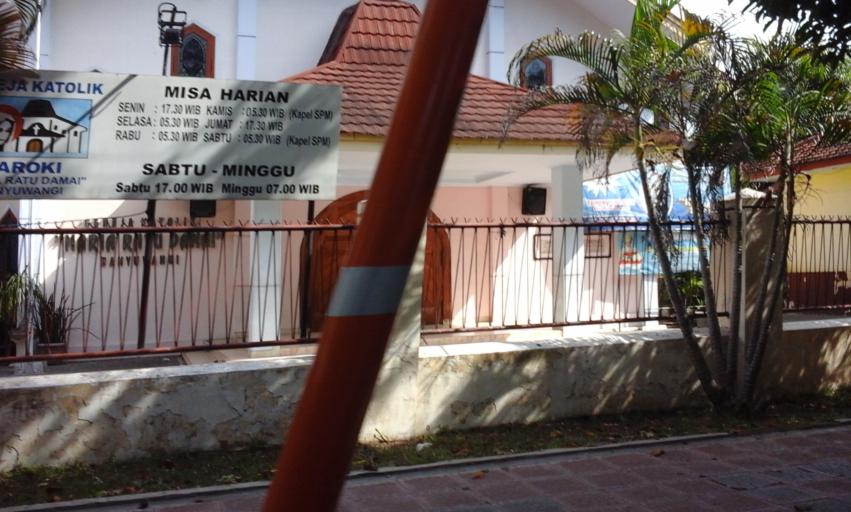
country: ID
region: East Java
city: Banyuwangi
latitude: -8.2164
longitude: 114.3639
